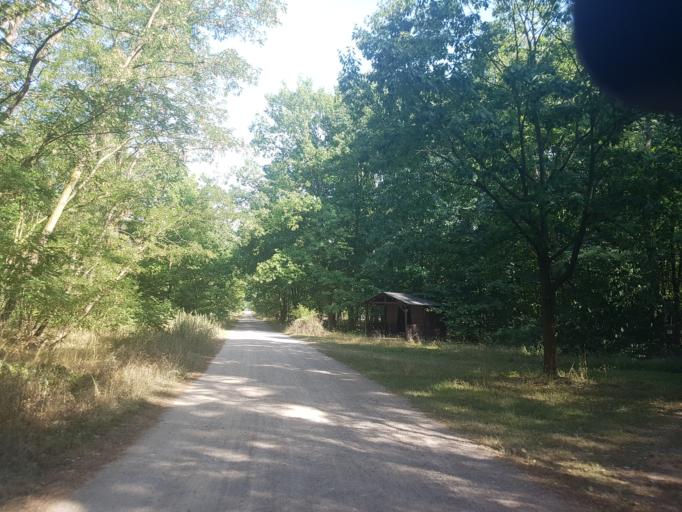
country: DE
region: Saxony-Anhalt
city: Seyda
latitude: 51.8769
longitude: 12.9557
